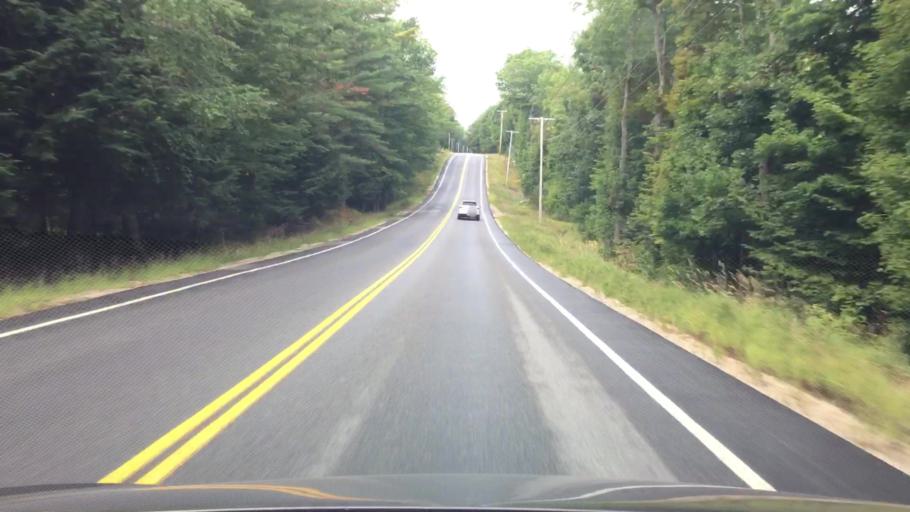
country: US
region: Maine
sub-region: Oxford County
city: Hartford
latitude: 44.3658
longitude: -70.3200
